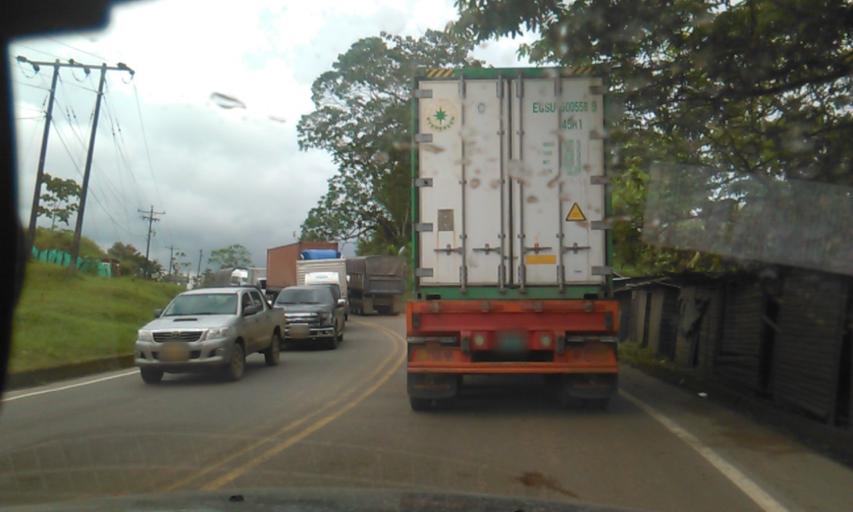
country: CO
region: Valle del Cauca
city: Buenaventura
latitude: 3.8799
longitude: -76.9356
